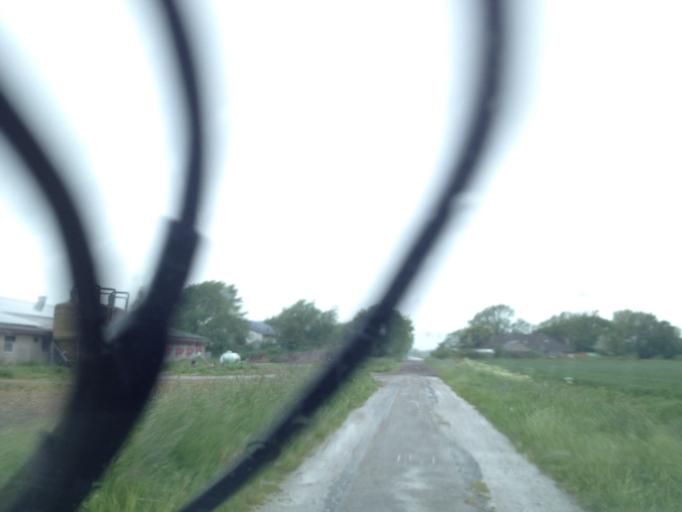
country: DE
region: Schleswig-Holstein
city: Klanxbull
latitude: 54.8862
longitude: 8.6912
